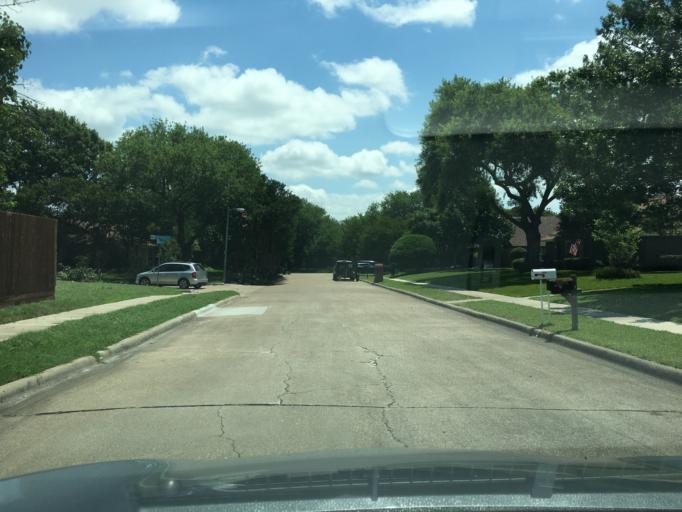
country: US
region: Texas
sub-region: Dallas County
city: Richardson
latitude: 32.9688
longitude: -96.6857
